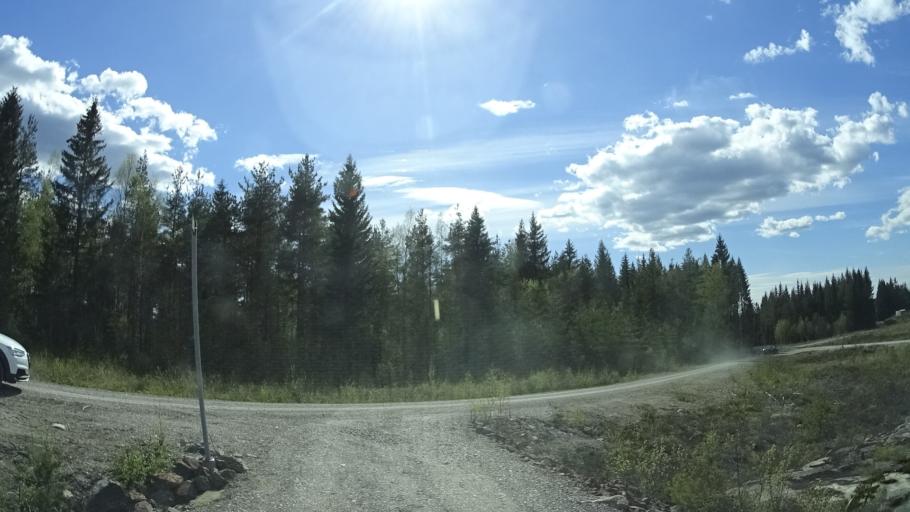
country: SE
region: OErebro
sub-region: Orebro Kommun
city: Garphyttan
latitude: 59.4147
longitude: 14.8847
